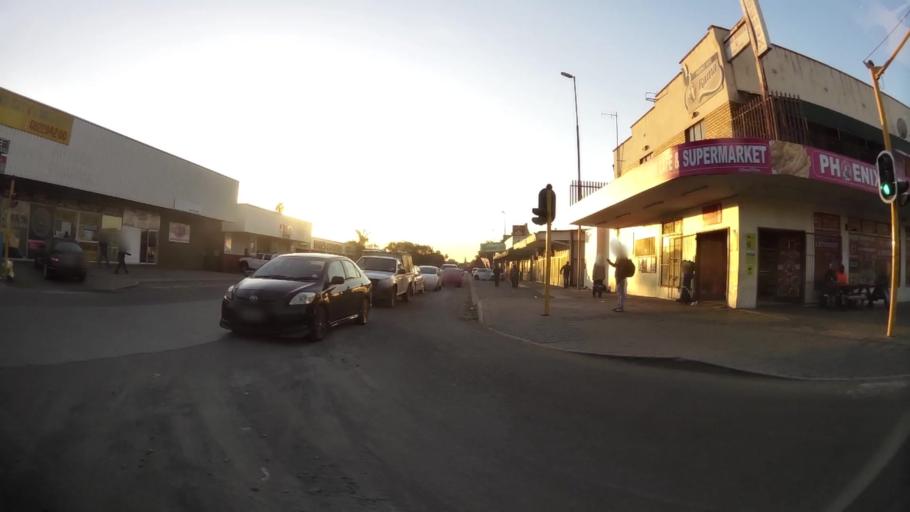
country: ZA
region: North-West
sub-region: Bojanala Platinum District Municipality
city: Rustenburg
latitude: -25.6623
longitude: 27.2463
